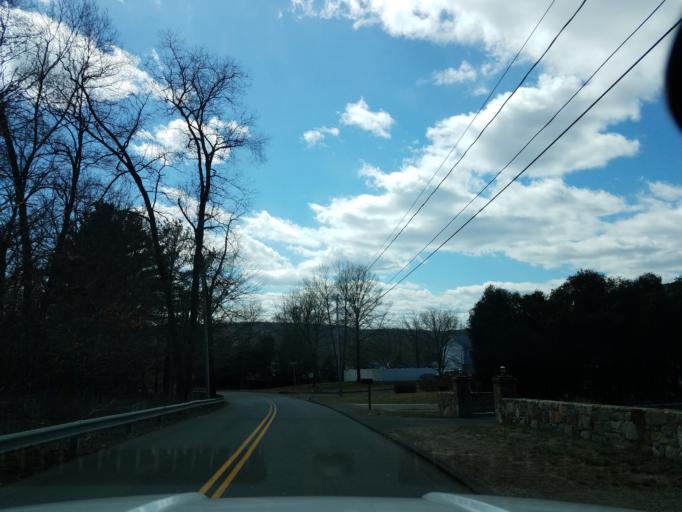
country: US
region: Connecticut
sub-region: New Haven County
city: Naugatuck
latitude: 41.4726
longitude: -73.0217
